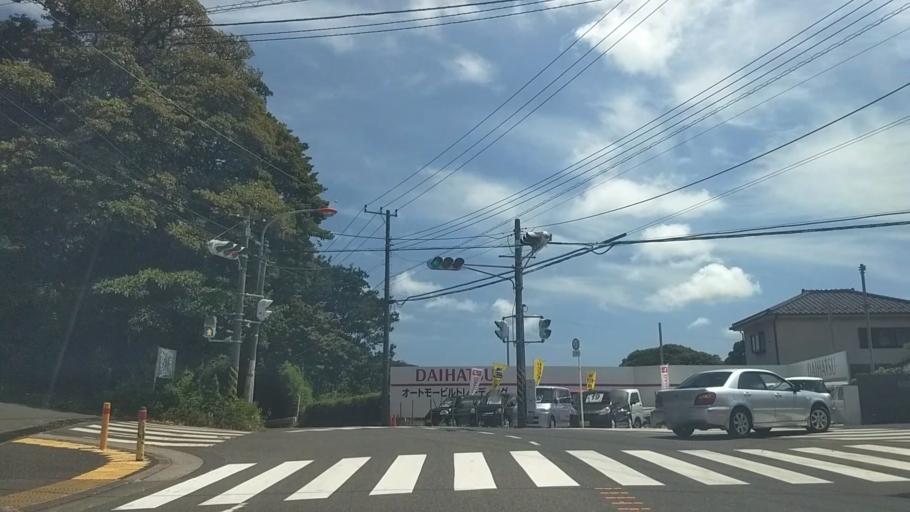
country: JP
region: Kanagawa
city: Miura
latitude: 35.2067
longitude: 139.6476
